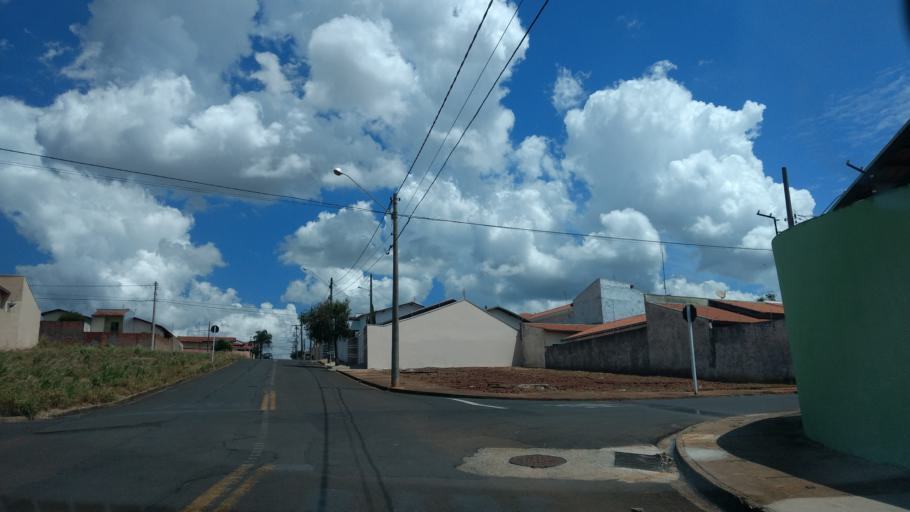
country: BR
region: Sao Paulo
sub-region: Botucatu
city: Botucatu
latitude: -22.8634
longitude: -48.4547
